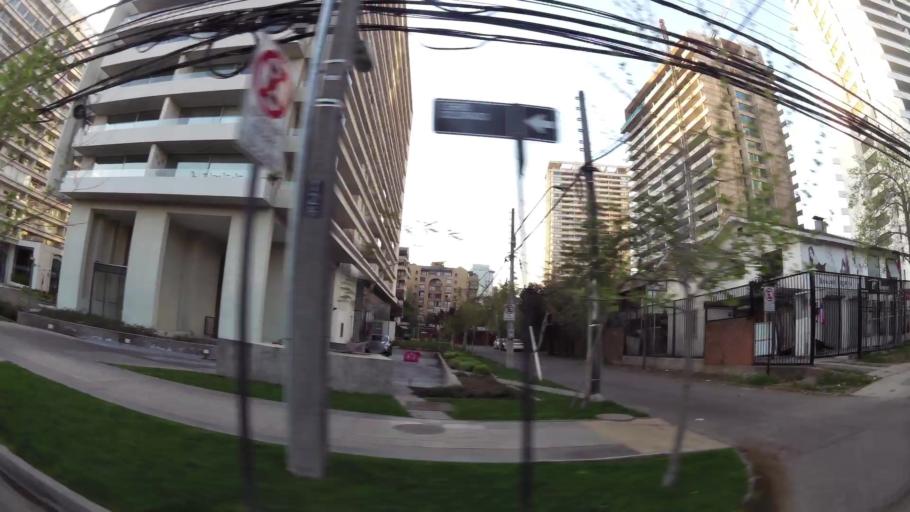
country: CL
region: Santiago Metropolitan
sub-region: Provincia de Santiago
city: Villa Presidente Frei, Nunoa, Santiago, Chile
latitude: -33.4011
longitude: -70.5728
